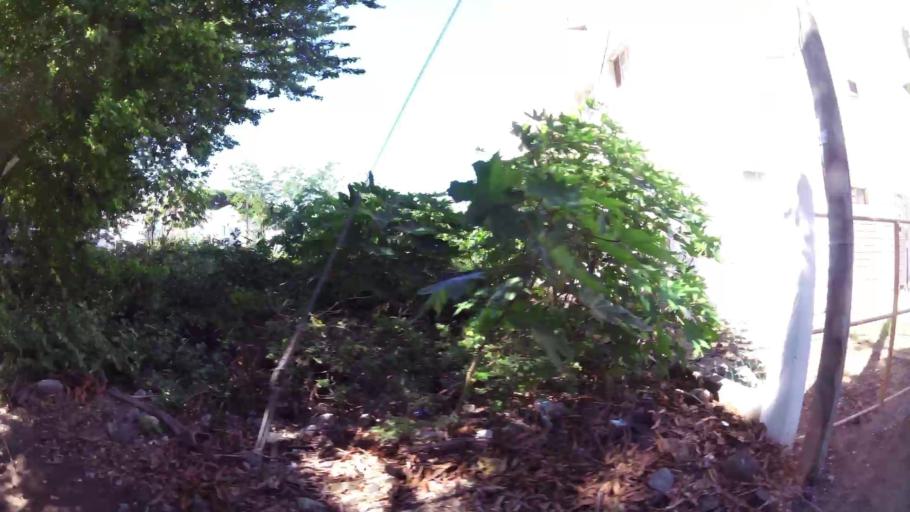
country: MU
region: Black River
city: Flic en Flac
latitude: -20.2768
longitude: 57.3703
